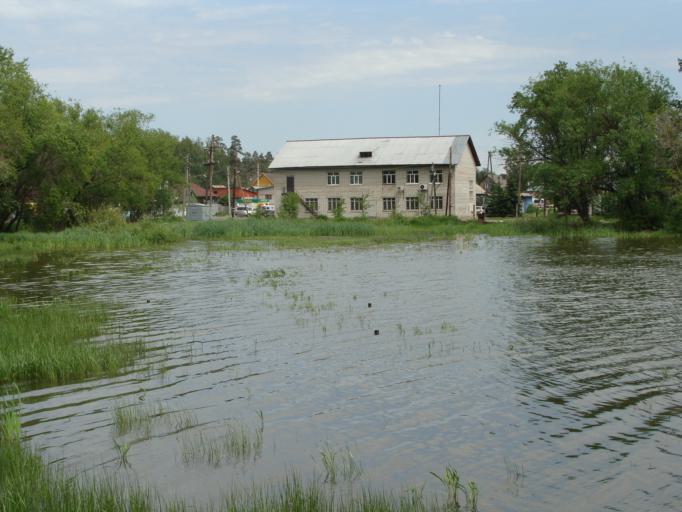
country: RU
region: Altai Krai
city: Lebyazh'ye
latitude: 53.2487
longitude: 83.6632
